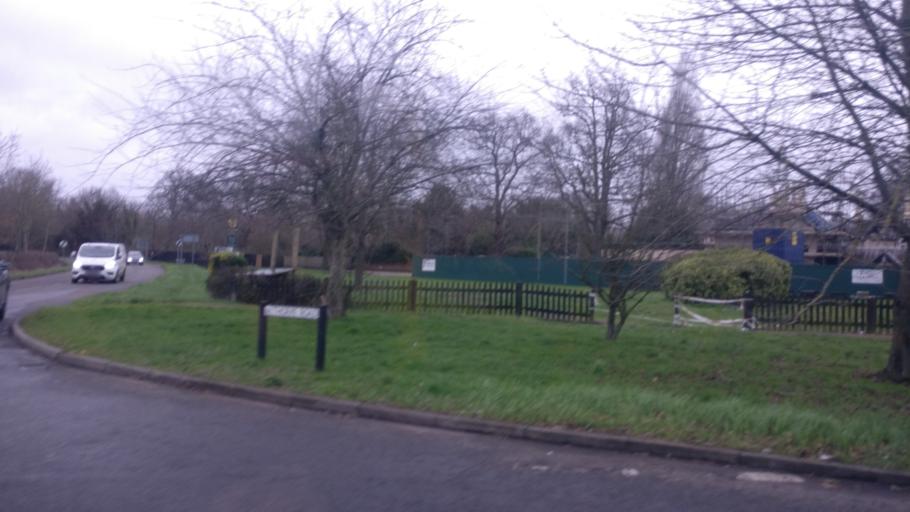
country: GB
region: England
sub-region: Surrey
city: Chertsey
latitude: 51.3941
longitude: -0.5163
